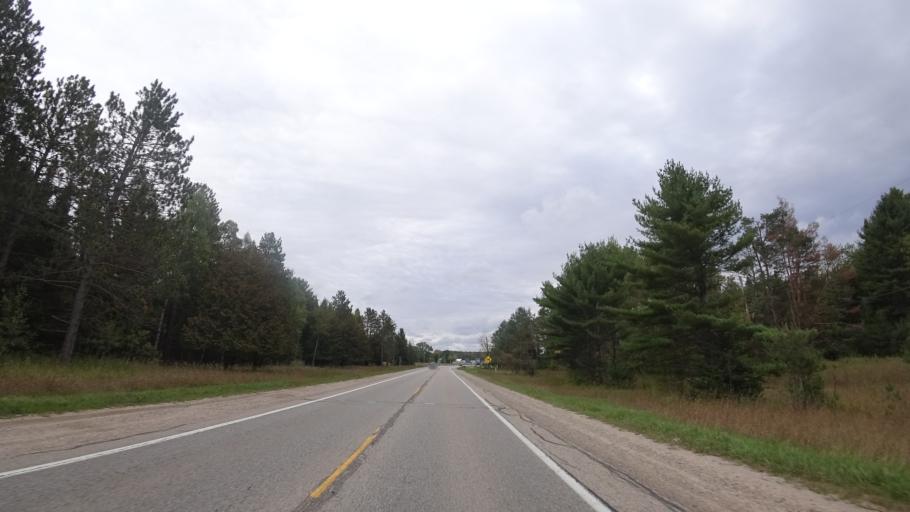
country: US
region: Michigan
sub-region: Charlevoix County
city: Boyne City
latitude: 45.1780
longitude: -84.9141
